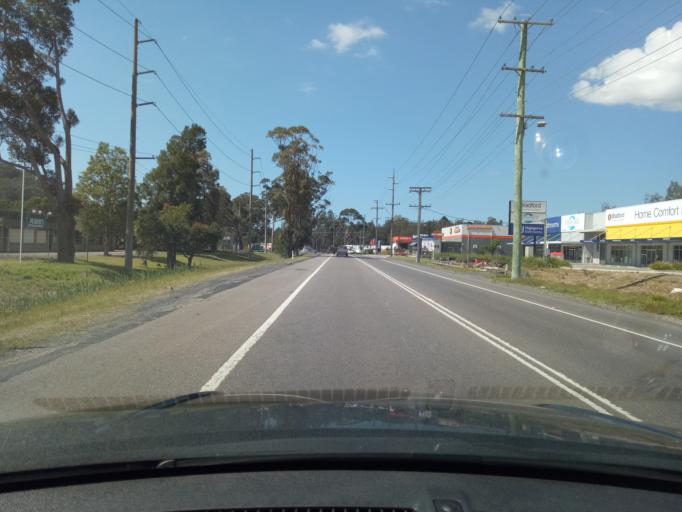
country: AU
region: New South Wales
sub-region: Gosford Shire
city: Gosford
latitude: -33.4157
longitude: 151.3301
